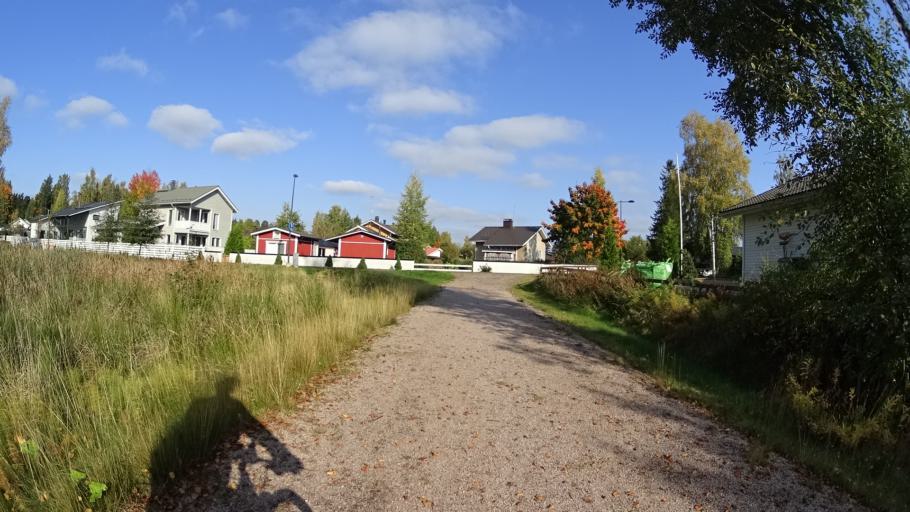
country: FI
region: Uusimaa
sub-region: Helsinki
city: Kilo
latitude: 60.2341
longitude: 24.8050
